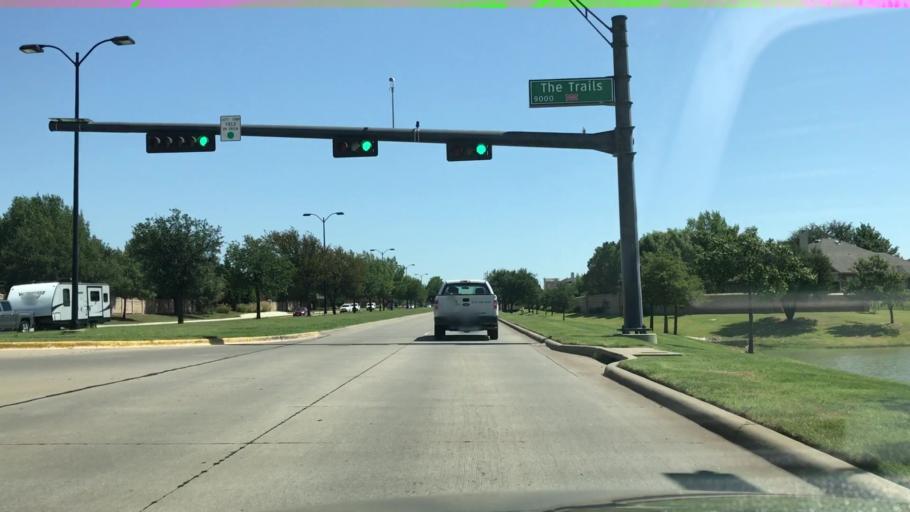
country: US
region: Texas
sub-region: Collin County
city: Frisco
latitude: 33.1532
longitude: -96.8721
